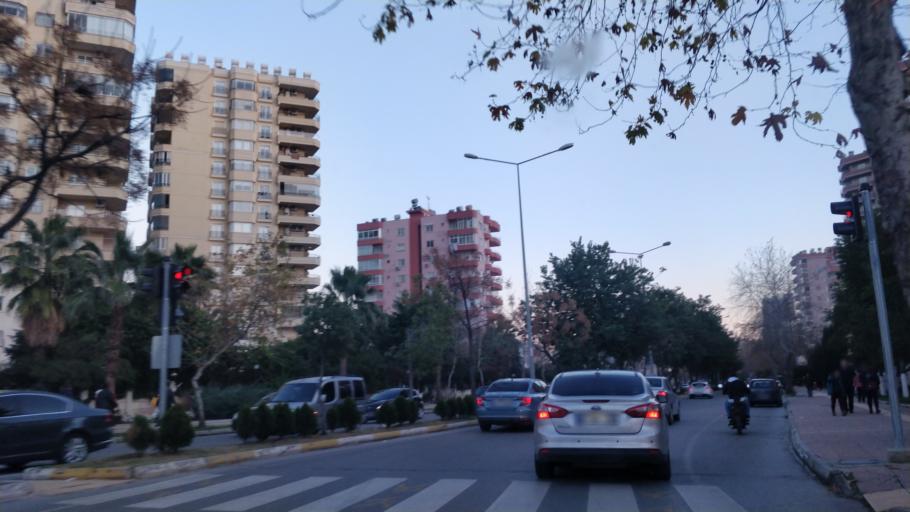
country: TR
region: Mersin
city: Mercin
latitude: 36.7902
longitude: 34.5922
